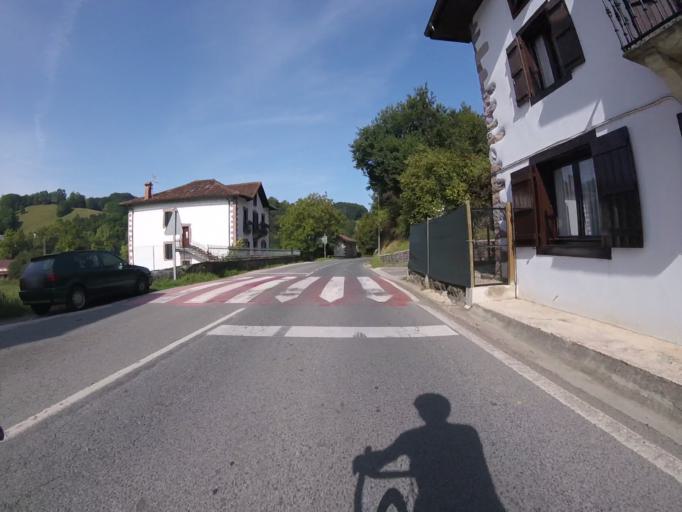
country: ES
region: Navarre
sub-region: Provincia de Navarra
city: Doneztebe
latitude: 43.1311
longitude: -1.5494
